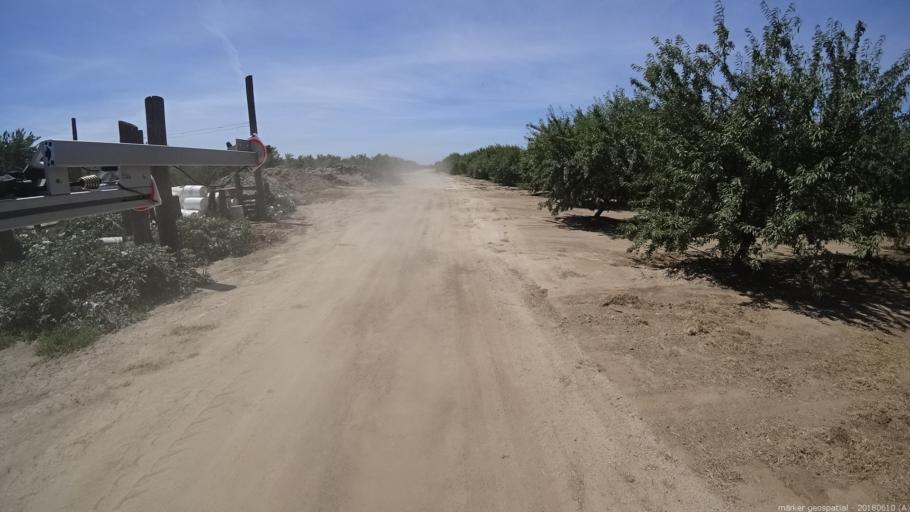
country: US
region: California
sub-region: Madera County
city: Chowchilla
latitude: 37.0392
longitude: -120.4195
